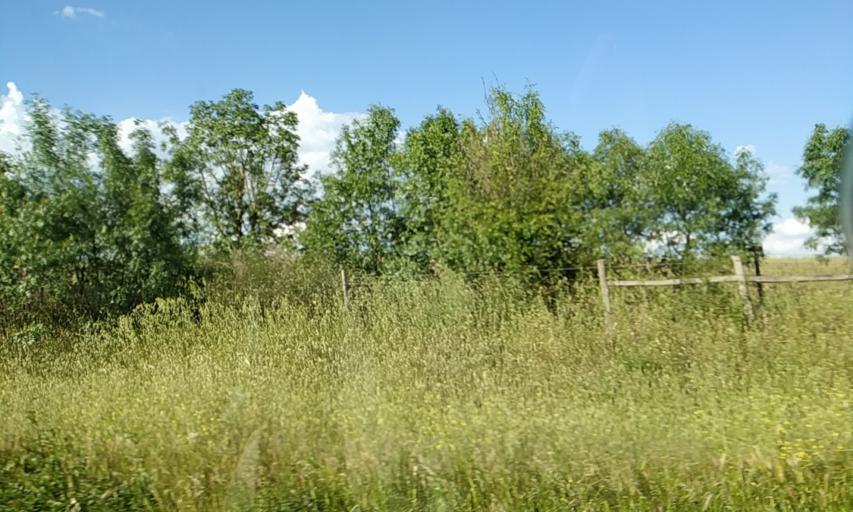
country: PT
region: Portalegre
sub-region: Portalegre
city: Urra
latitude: 39.1222
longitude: -7.4438
